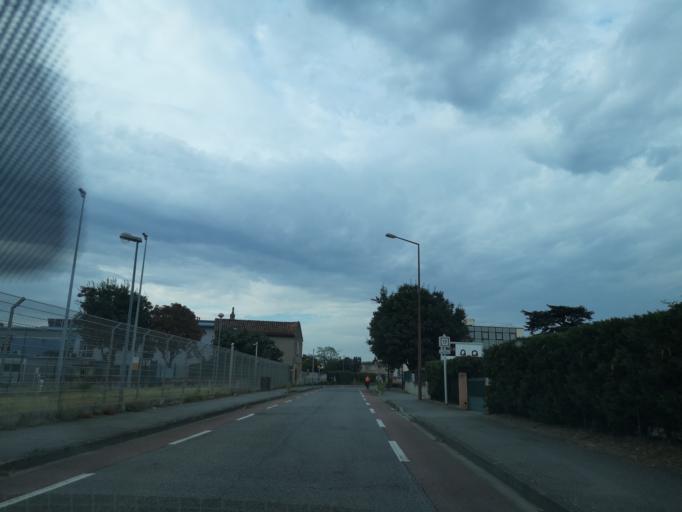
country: FR
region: Midi-Pyrenees
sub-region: Departement de la Haute-Garonne
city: Portet-sur-Garonne
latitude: 43.5654
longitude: 1.3890
